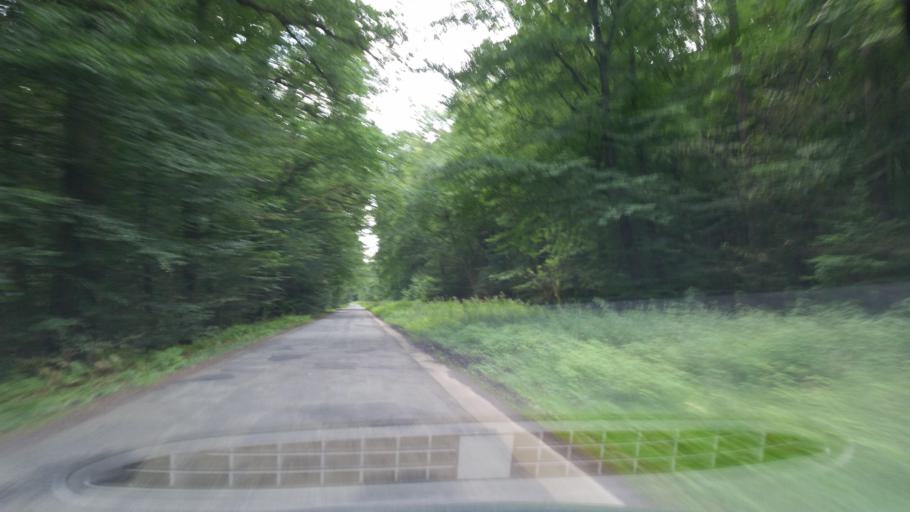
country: DE
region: Lower Saxony
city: Bispingen
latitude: 53.0945
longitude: 9.9070
